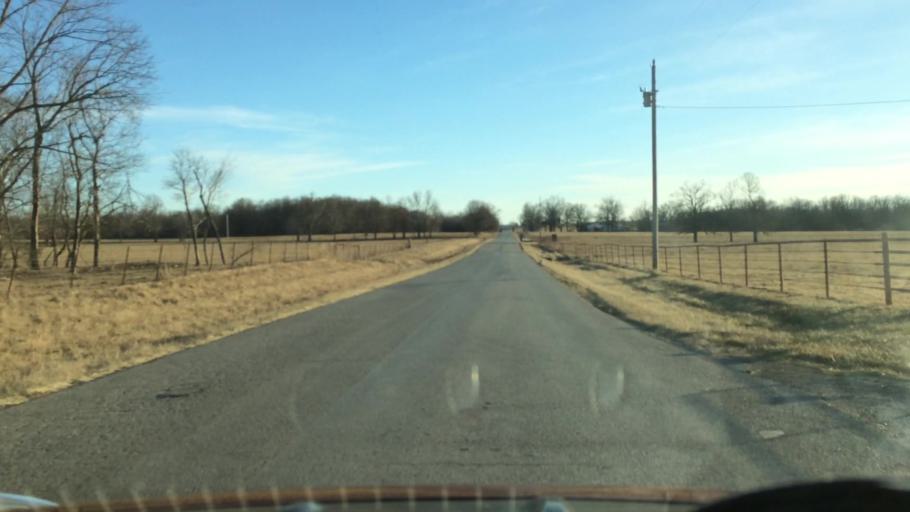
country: US
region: Missouri
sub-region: Webster County
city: Marshfield
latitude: 37.3339
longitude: -92.9840
